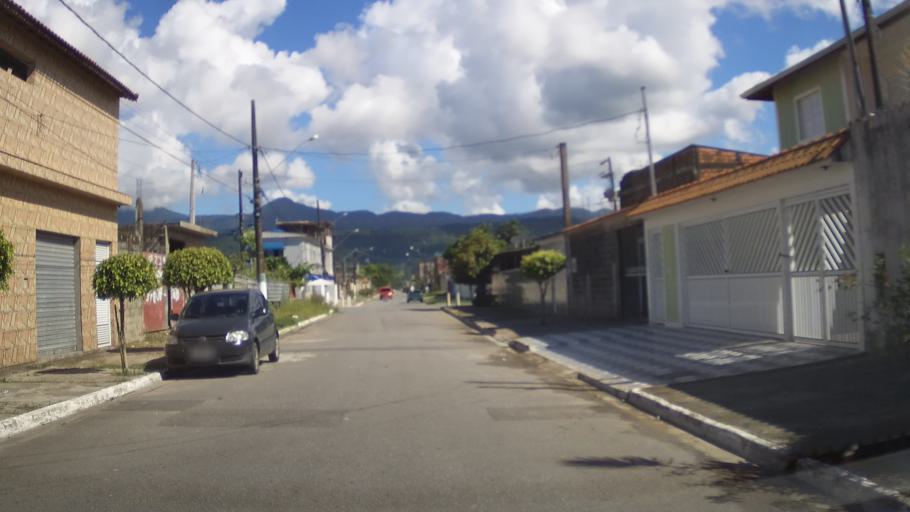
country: BR
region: Sao Paulo
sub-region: Praia Grande
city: Praia Grande
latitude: -24.0220
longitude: -46.5088
